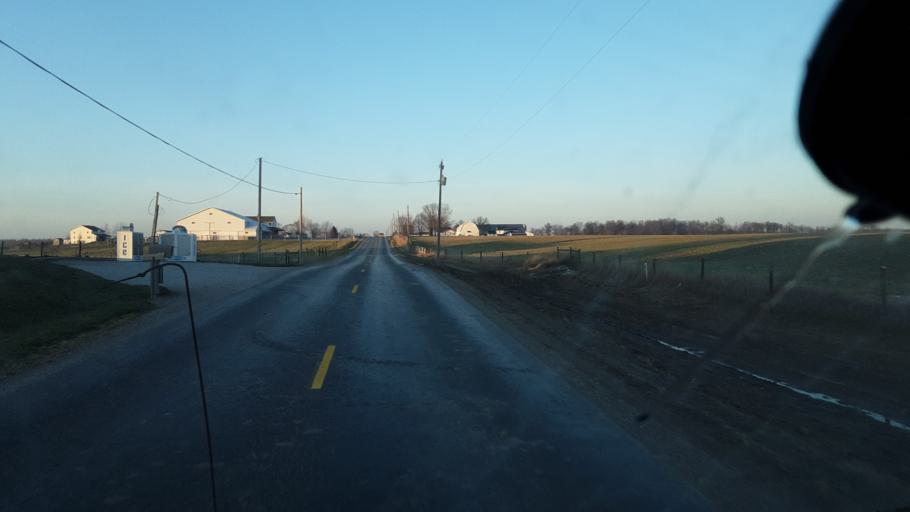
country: US
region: Indiana
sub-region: Allen County
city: Grabill
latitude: 41.2135
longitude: -84.9419
